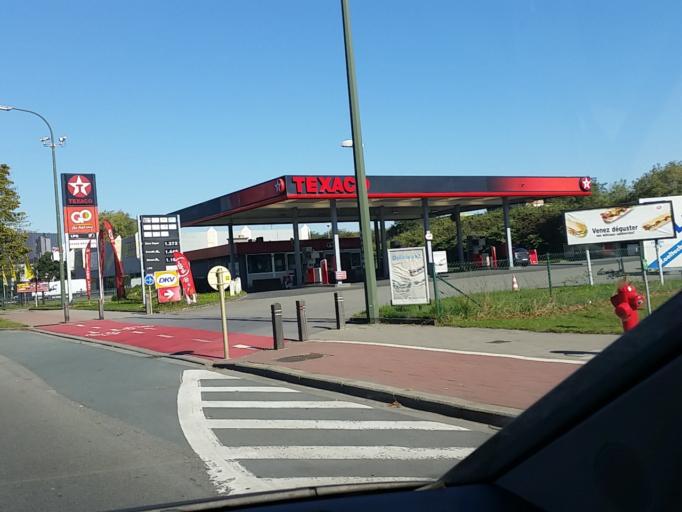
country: BE
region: Flanders
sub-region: Provincie Vlaams-Brabant
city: Drogenbos
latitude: 50.8154
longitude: 4.3076
